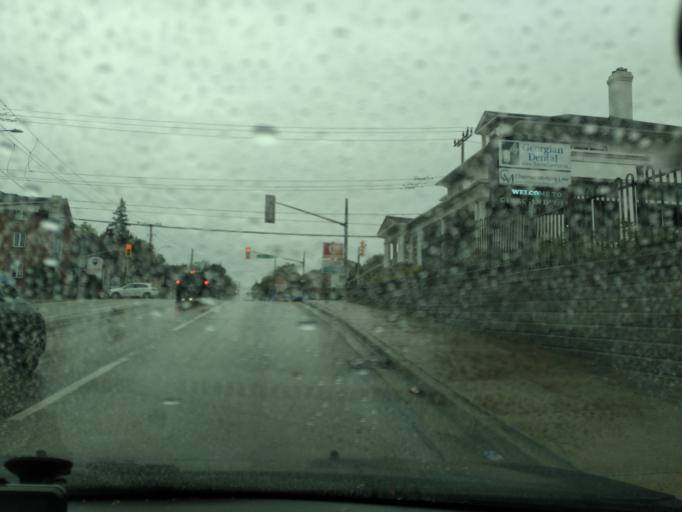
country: CA
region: Ontario
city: Barrie
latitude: 44.3934
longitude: -79.6936
